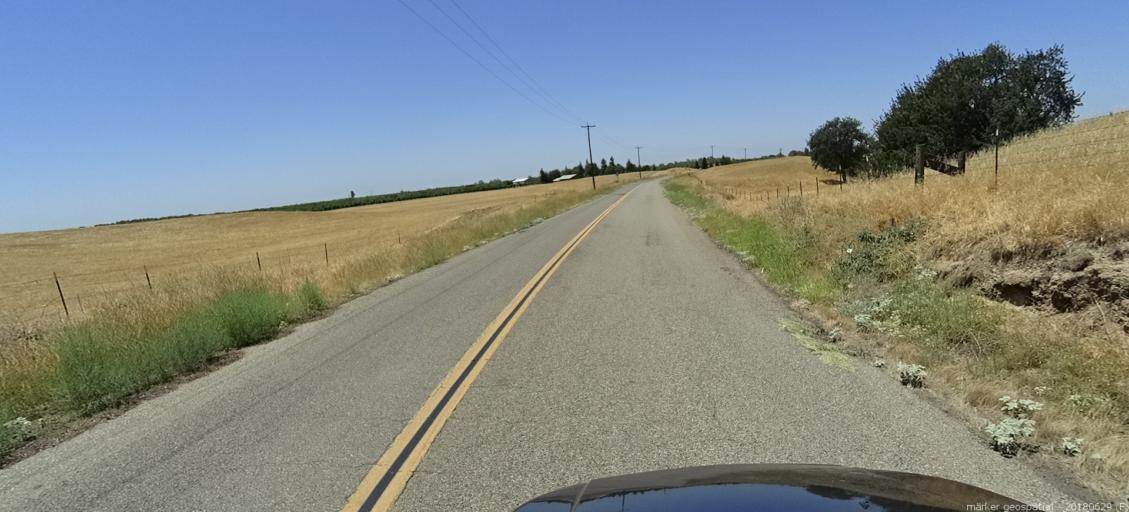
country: US
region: California
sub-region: Madera County
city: Parksdale
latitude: 37.0137
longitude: -119.9618
